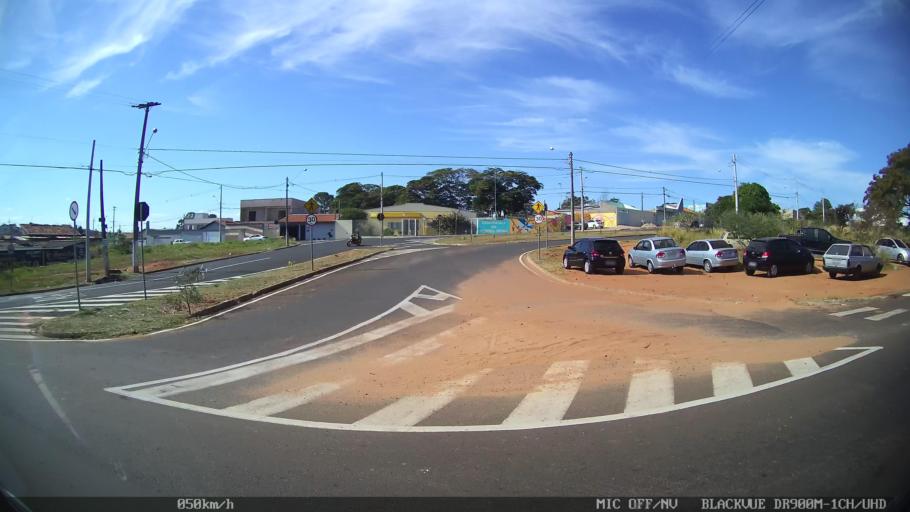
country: BR
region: Sao Paulo
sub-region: Franca
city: Franca
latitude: -20.5206
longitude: -47.4361
